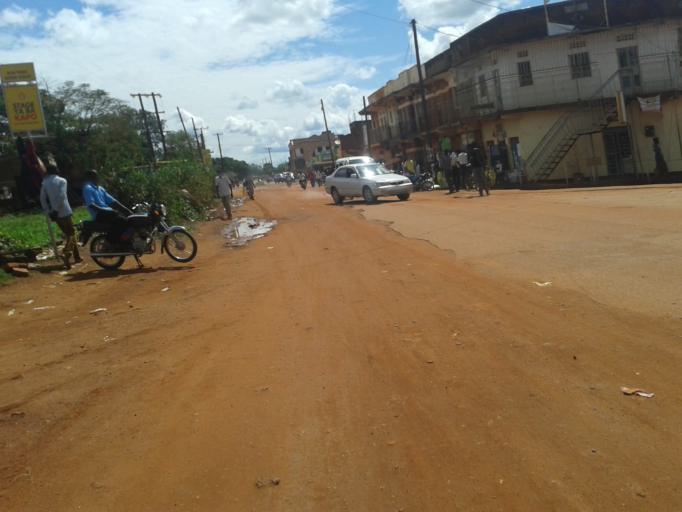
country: UG
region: Northern Region
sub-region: Gulu District
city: Gulu
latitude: 2.7701
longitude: 32.3001
